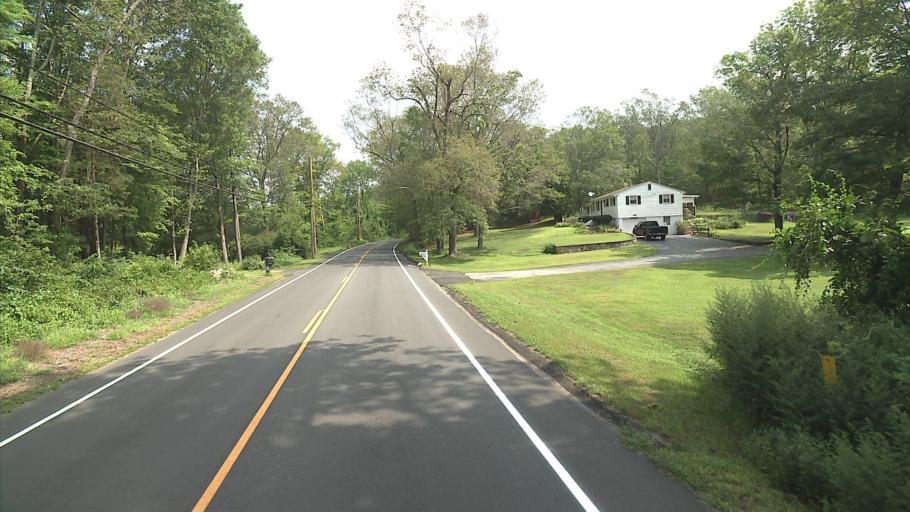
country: US
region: Connecticut
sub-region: New London County
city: Montville Center
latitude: 41.4872
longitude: -72.2507
